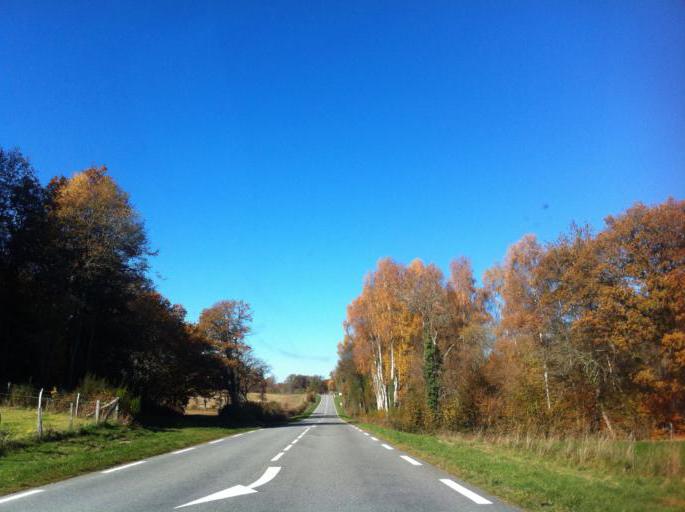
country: FR
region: Auvergne
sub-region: Departement du Puy-de-Dome
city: Gelles
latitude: 45.8607
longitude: 2.6055
